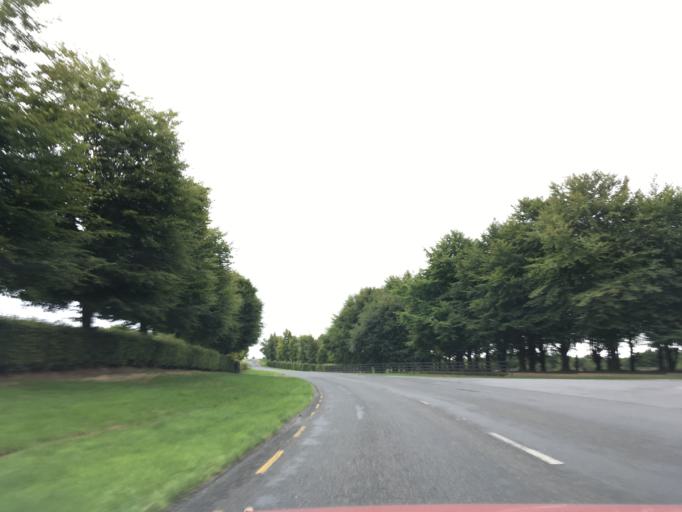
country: IE
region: Munster
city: Cashel
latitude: 52.4618
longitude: -7.8267
